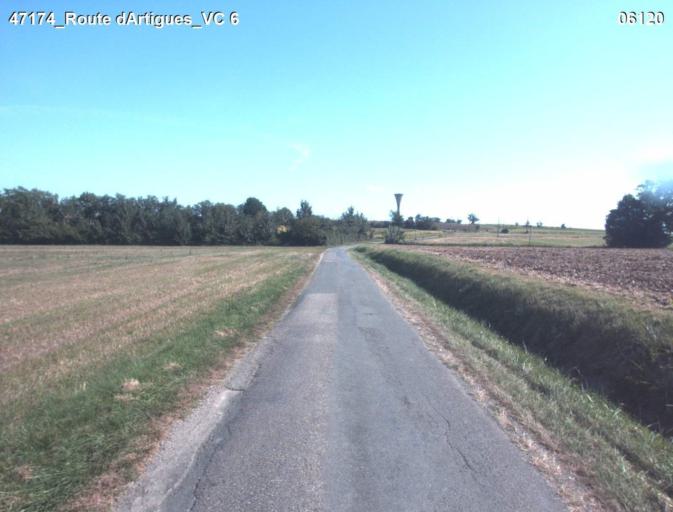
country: FR
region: Aquitaine
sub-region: Departement du Lot-et-Garonne
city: Mezin
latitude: 44.0534
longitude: 0.3313
